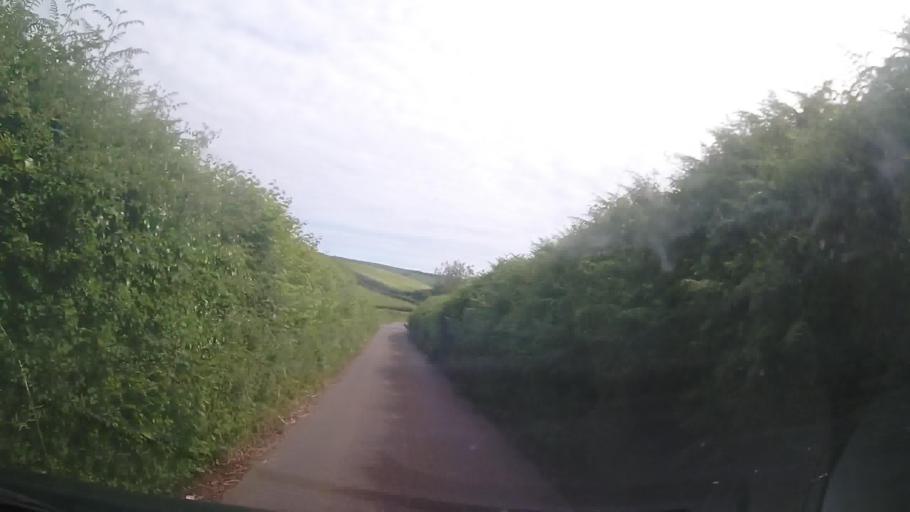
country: GB
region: England
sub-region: Devon
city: Salcombe
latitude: 50.2413
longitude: -3.6789
